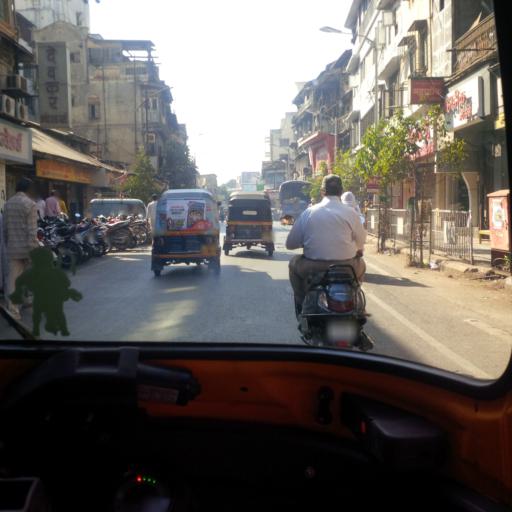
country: IN
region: Maharashtra
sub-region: Pune Division
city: Pune
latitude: 18.5160
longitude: 73.8589
